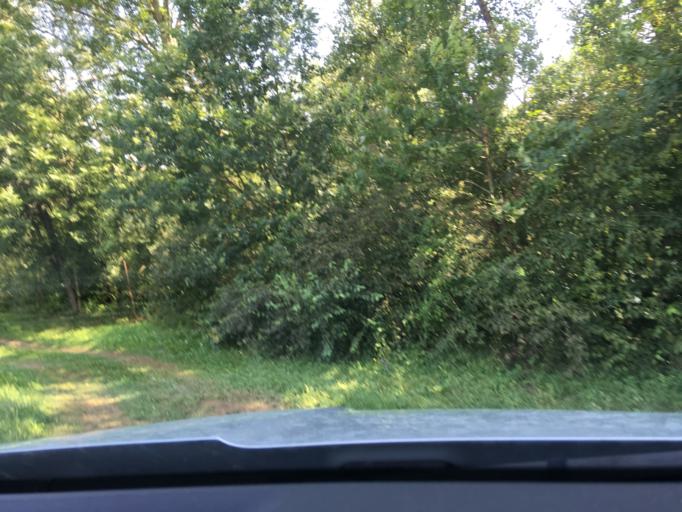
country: SI
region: Metlika
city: Metlika
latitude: 45.6453
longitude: 15.3611
